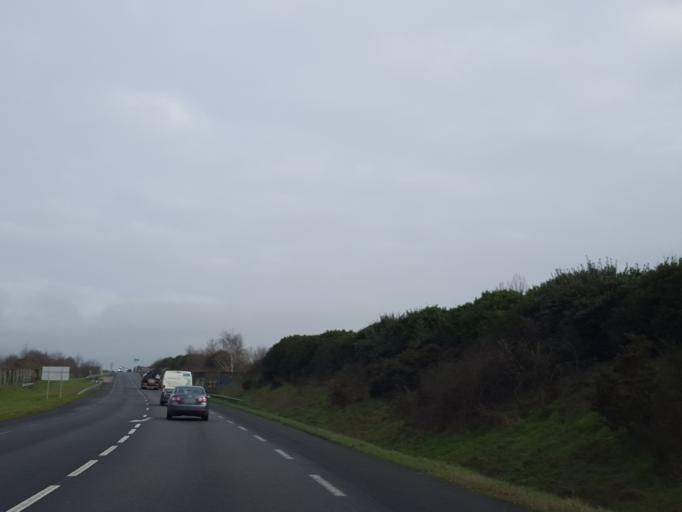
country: FR
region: Pays de la Loire
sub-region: Departement de la Vendee
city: La Roche-sur-Yon
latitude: 46.6693
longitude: -1.4600
